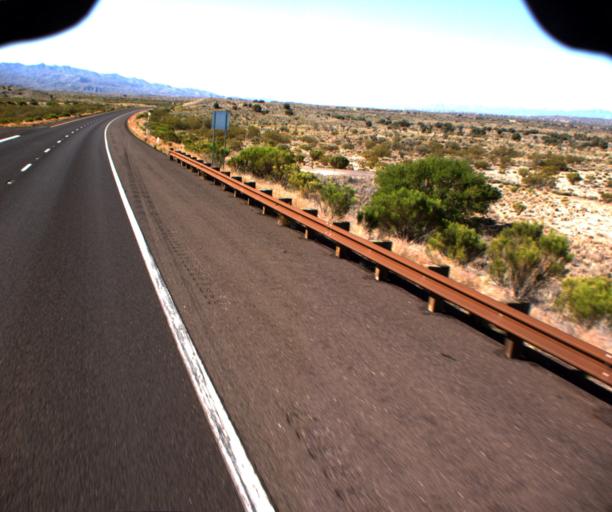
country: US
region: Arizona
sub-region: Mohave County
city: New Kingman-Butler
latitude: 35.1311
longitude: -113.6683
